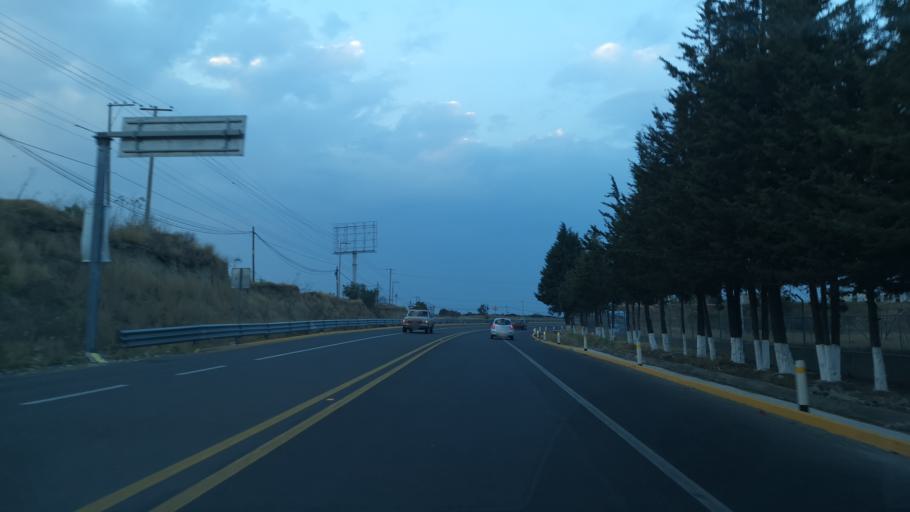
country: MX
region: Puebla
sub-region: Huejotzingo
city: Los Encinos
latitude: 19.1674
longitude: -98.3776
